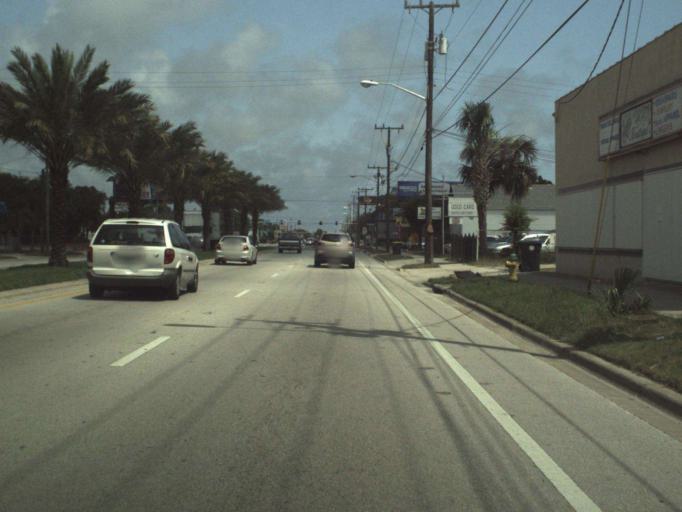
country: US
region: Florida
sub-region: Volusia County
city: Daytona Beach
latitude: 29.2240
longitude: -81.0297
